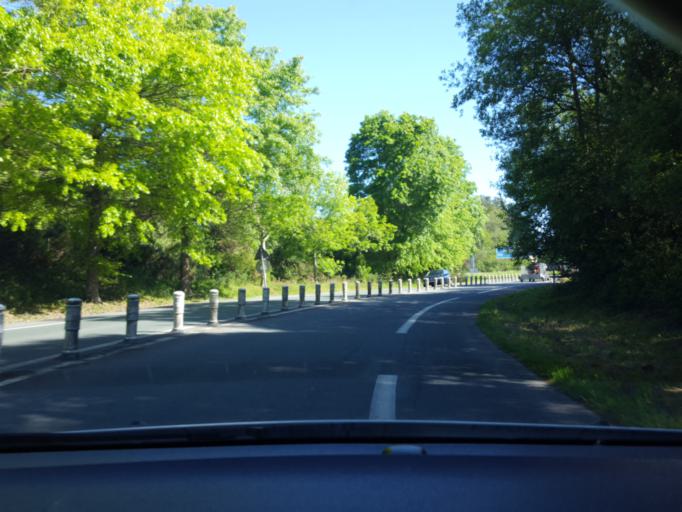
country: FR
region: Aquitaine
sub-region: Departement des Landes
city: Ondres
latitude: 43.5426
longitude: -1.4377
